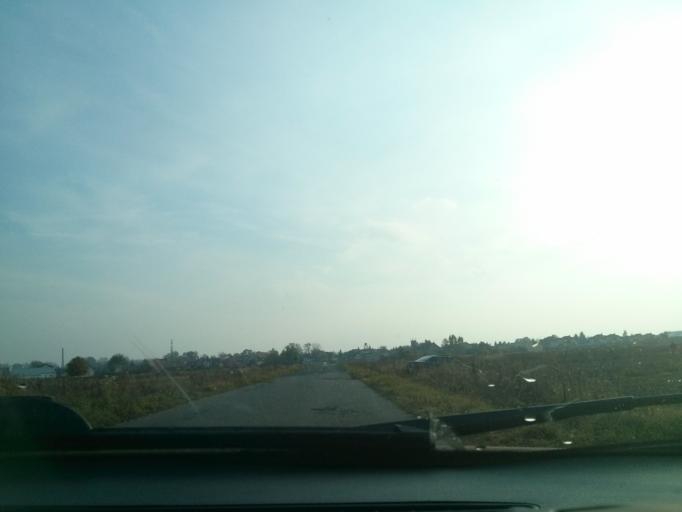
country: PL
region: Masovian Voivodeship
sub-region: Powiat piaseczynski
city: Konstancin-Jeziorna
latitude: 52.1139
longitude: 21.1330
